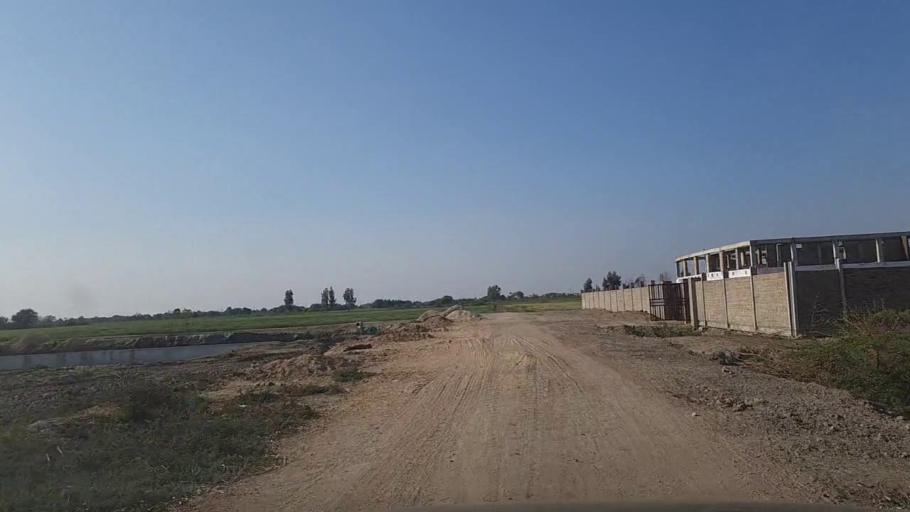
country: PK
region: Sindh
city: Digri
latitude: 25.0280
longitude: 69.2242
